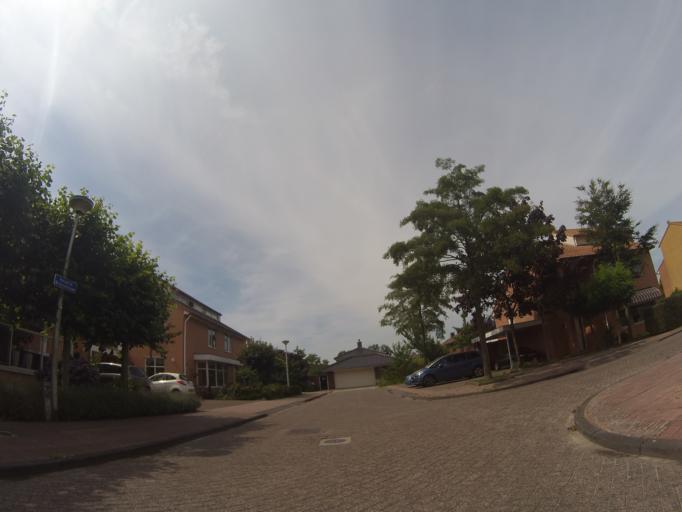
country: NL
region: Utrecht
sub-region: Gemeente Amersfoort
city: Randenbroek
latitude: 52.1849
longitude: 5.4292
